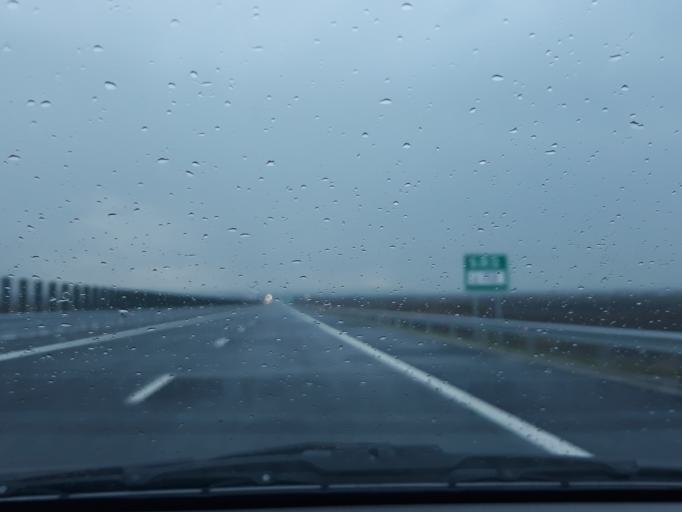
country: RO
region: Mures
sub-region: Comuna Ogra
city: Ogra
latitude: 46.4369
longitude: 24.3184
